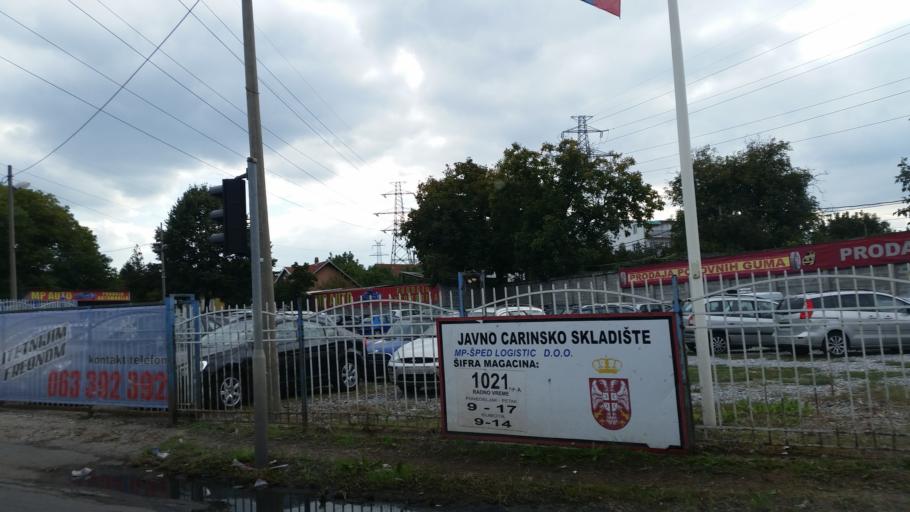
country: RS
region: Central Serbia
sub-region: Belgrade
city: Zemun
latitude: 44.8074
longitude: 20.3613
